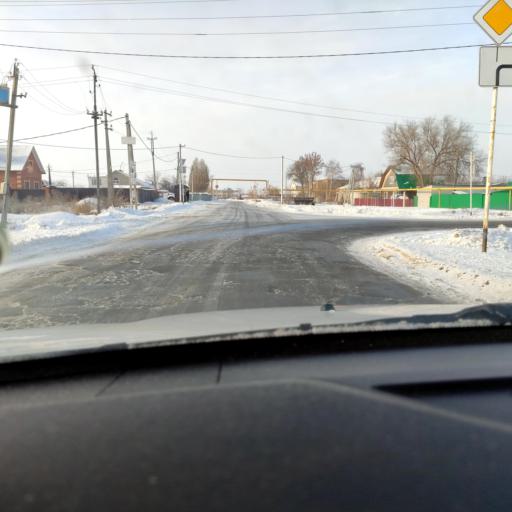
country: RU
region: Samara
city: Smyshlyayevka
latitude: 53.1602
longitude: 50.3828
